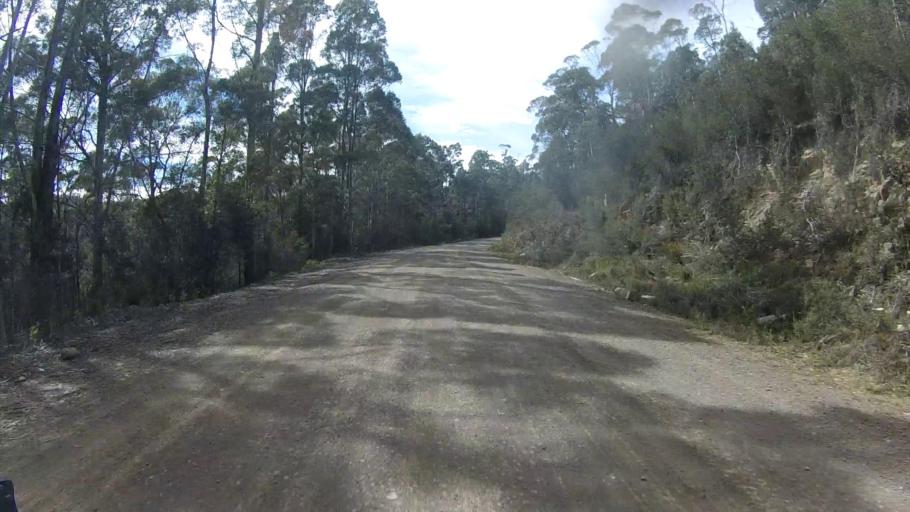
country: AU
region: Tasmania
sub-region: Sorell
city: Sorell
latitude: -42.6996
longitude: 147.8553
